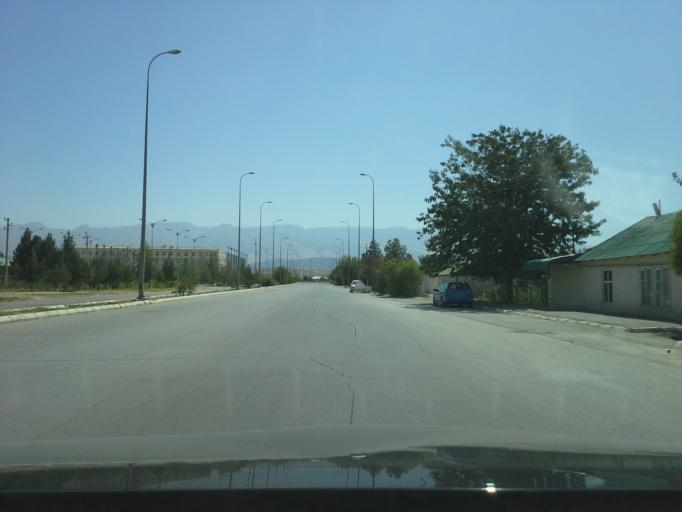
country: TM
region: Ahal
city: Ashgabat
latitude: 38.0046
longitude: 58.3039
